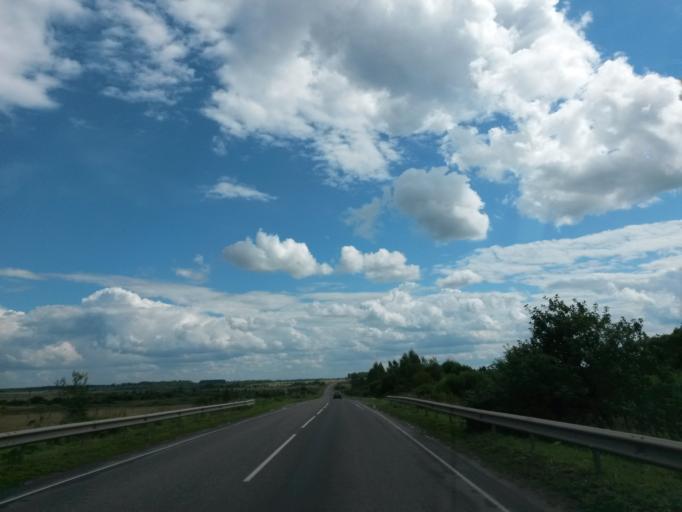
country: RU
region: Jaroslavl
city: Dubki
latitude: 57.1997
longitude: 40.3369
